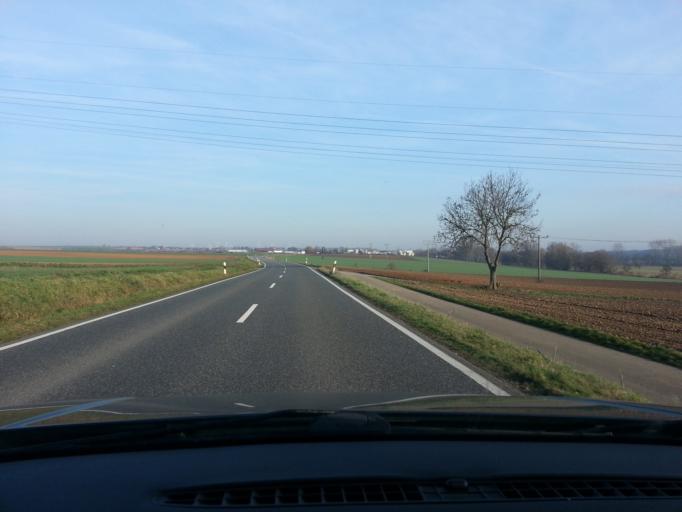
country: DE
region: Rheinland-Pfalz
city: Insheim
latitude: 49.1422
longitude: 8.1739
